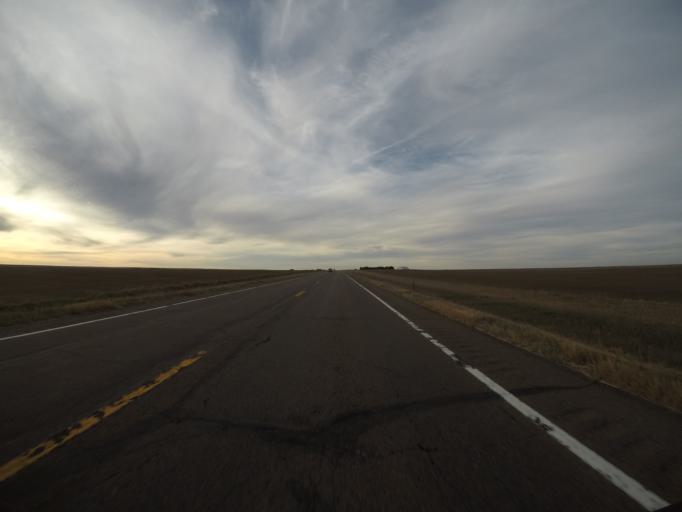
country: US
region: Colorado
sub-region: Yuma County
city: Yuma
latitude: 39.6812
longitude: -102.9669
